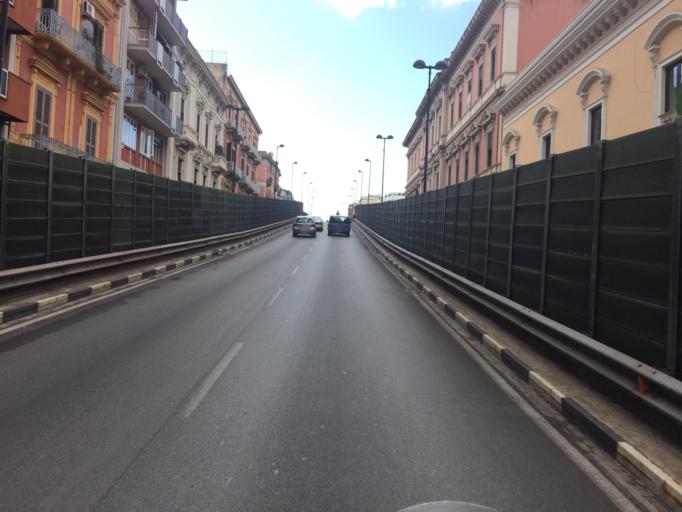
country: IT
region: Apulia
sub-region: Provincia di Bari
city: Bari
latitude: 41.1193
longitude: 16.8727
